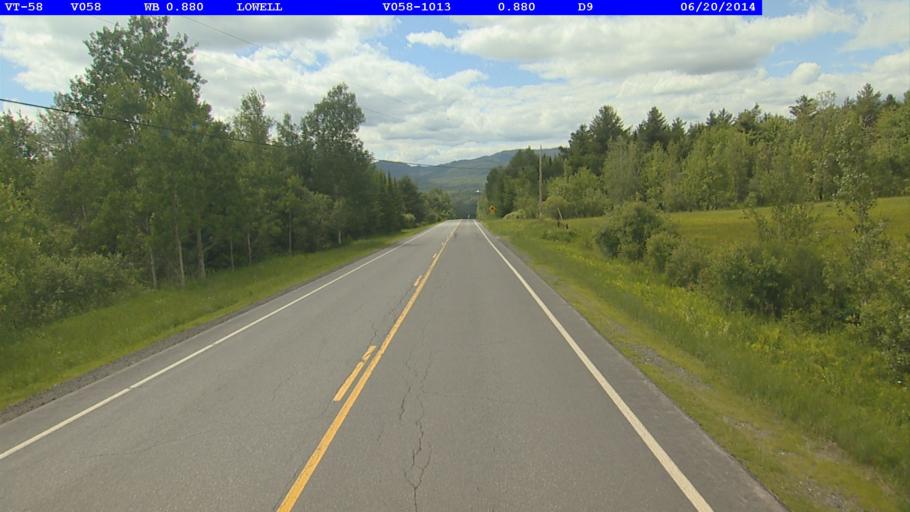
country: US
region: Vermont
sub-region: Orleans County
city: Newport
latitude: 44.7983
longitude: -72.4309
